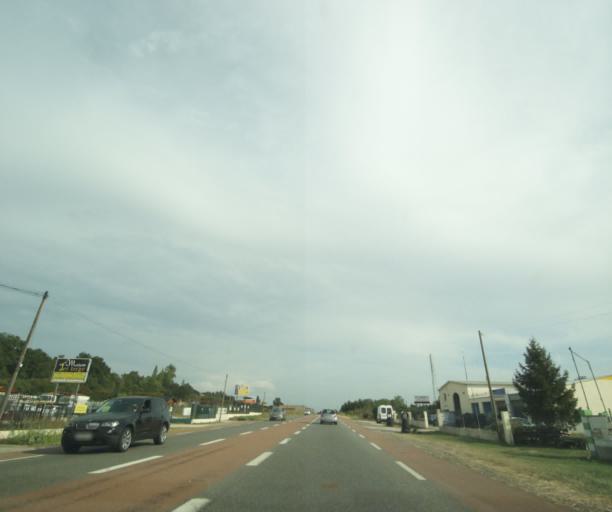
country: FR
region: Midi-Pyrenees
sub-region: Departement du Tarn-et-Garonne
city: Pompignan
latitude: 43.8098
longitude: 1.3191
